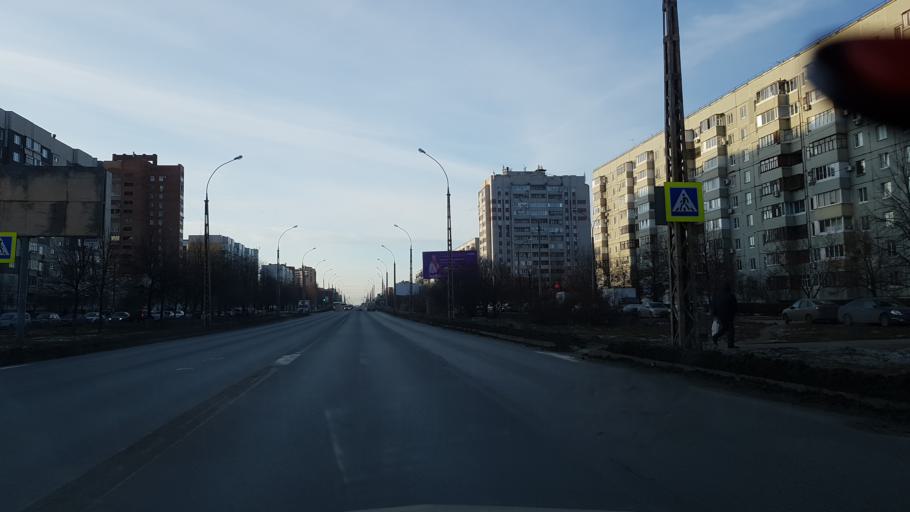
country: RU
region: Samara
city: Tol'yatti
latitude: 53.5402
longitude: 49.3555
